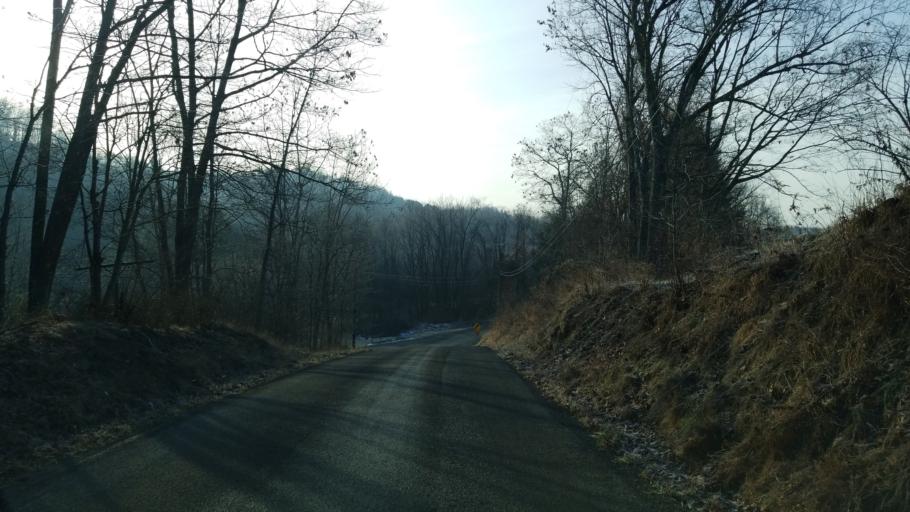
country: US
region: Pennsylvania
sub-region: Jefferson County
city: Brookville
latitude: 40.9598
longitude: -79.2576
